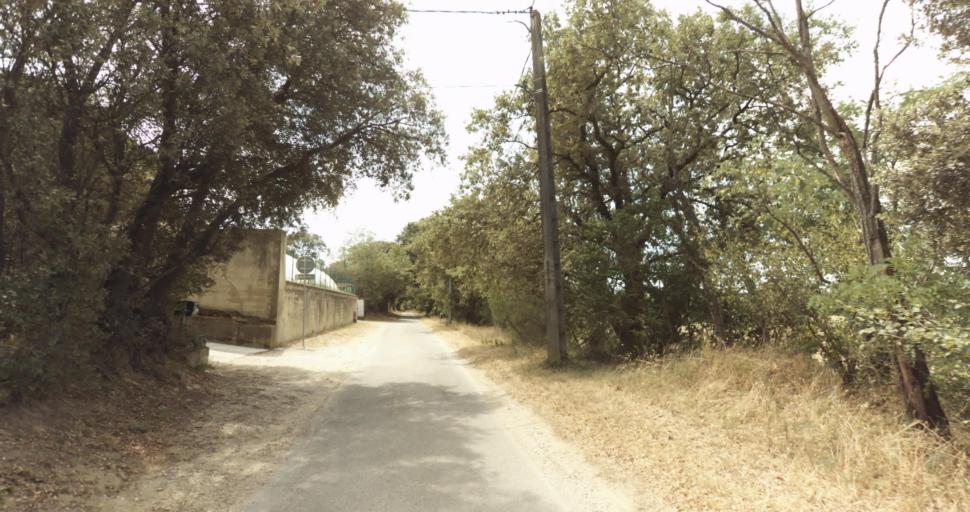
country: FR
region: Provence-Alpes-Cote d'Azur
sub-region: Departement du Vaucluse
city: Monteux
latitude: 44.0559
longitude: 4.9858
